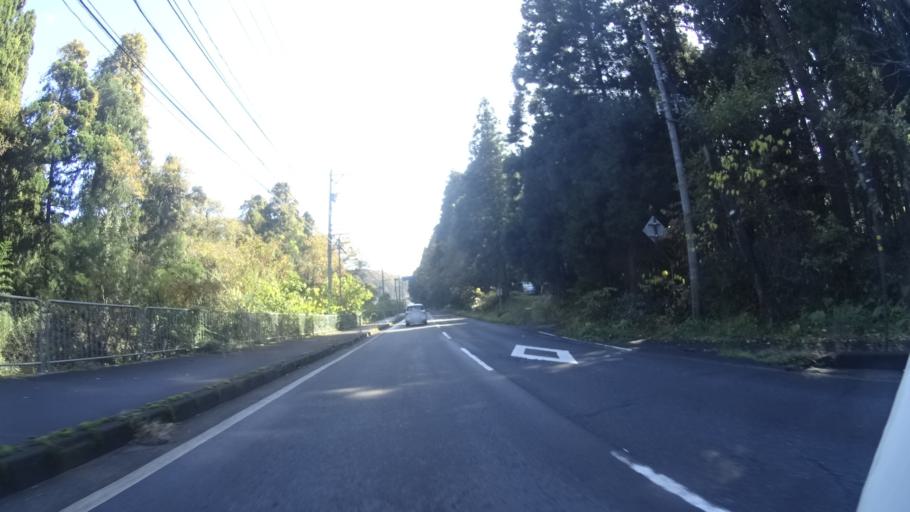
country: JP
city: Asahi
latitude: 35.9657
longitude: 136.1048
